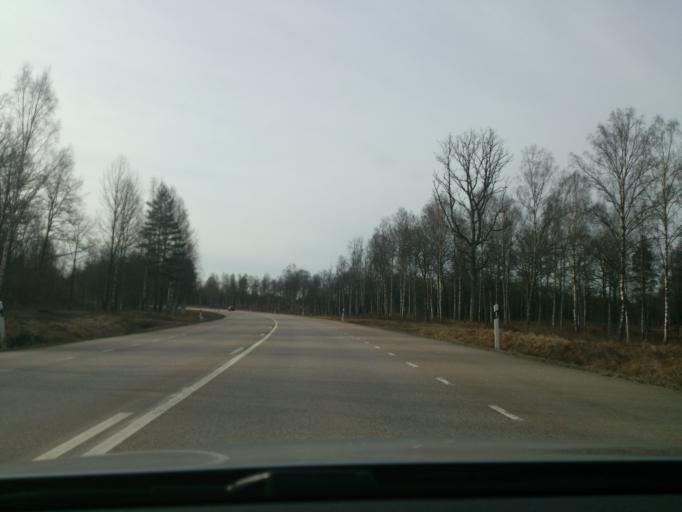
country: SE
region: Kronoberg
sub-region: Alvesta Kommun
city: Alvesta
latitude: 56.9170
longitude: 14.5540
